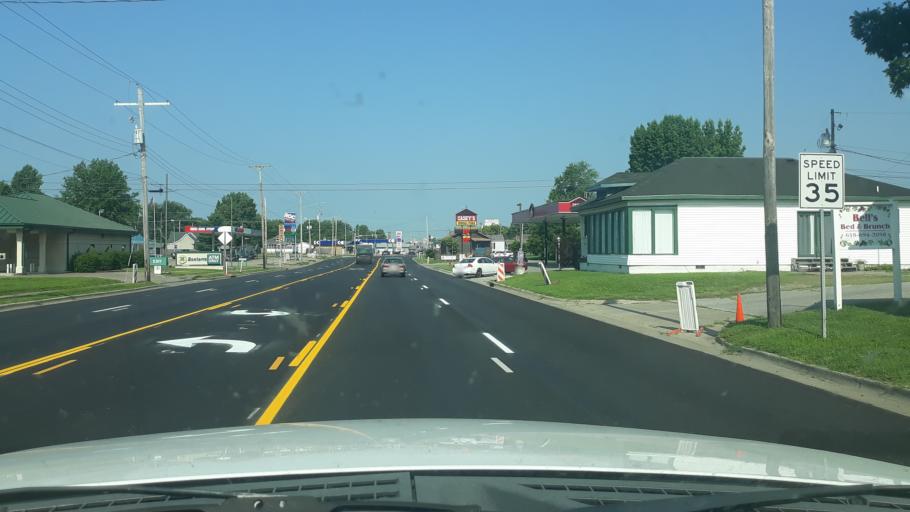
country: US
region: Illinois
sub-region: Williamson County
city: Marion
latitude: 37.7406
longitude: -88.9212
